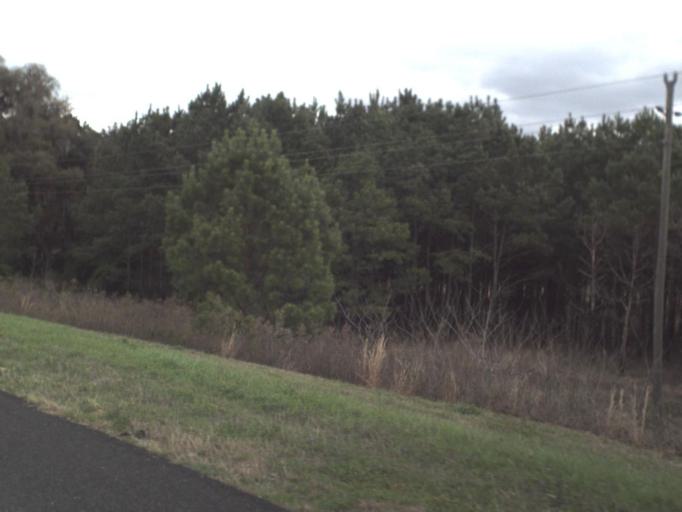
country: US
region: Florida
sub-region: Leon County
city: Tallahassee
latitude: 30.6219
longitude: -84.1701
